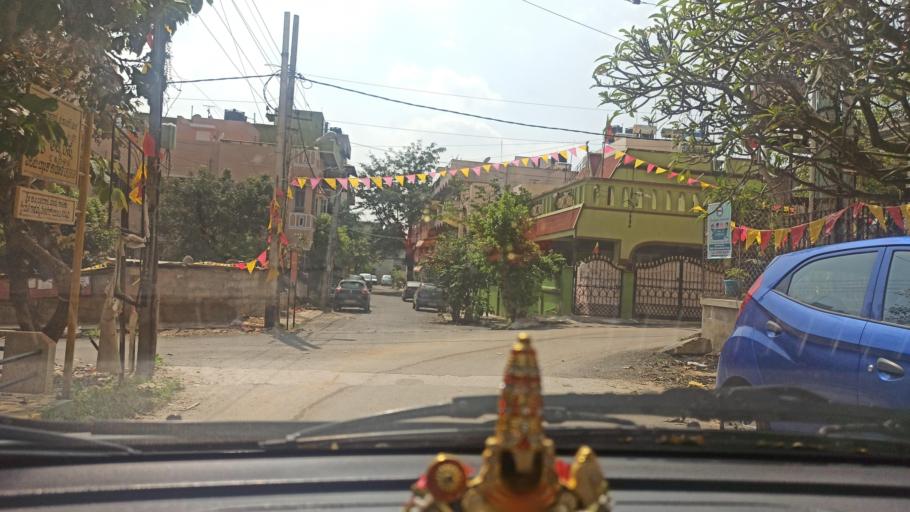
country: IN
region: Karnataka
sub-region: Bangalore Urban
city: Bangalore
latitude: 13.0181
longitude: 77.6617
